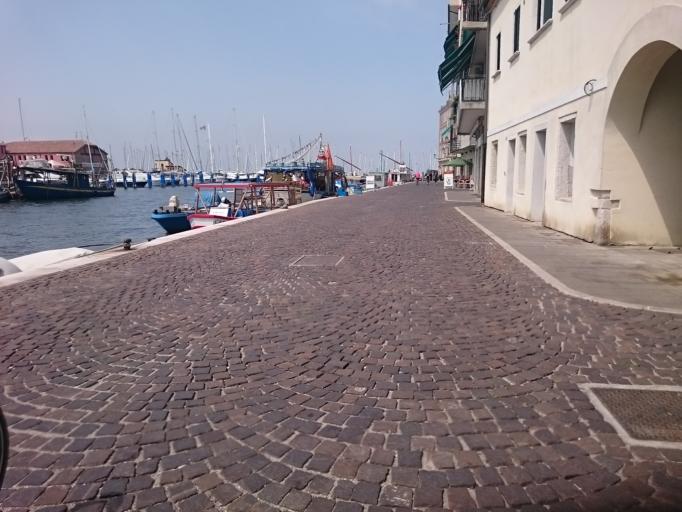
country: IT
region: Veneto
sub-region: Provincia di Venezia
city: Chioggia
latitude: 45.2229
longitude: 12.2784
